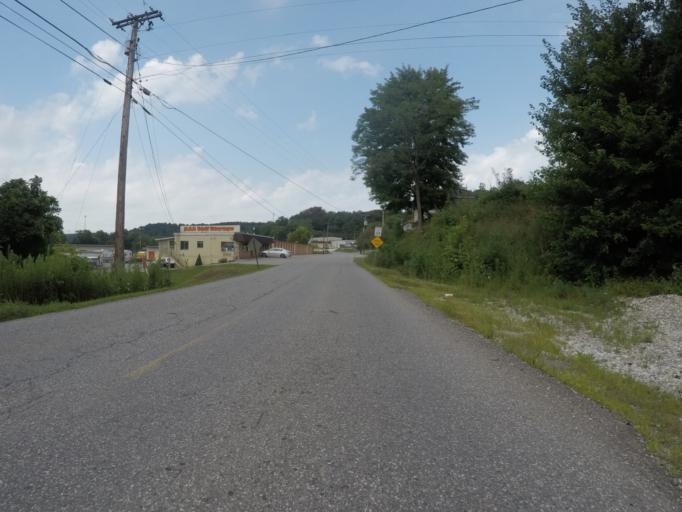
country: US
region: Kentucky
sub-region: Boyd County
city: Meads
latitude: 38.4183
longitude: -82.7057
